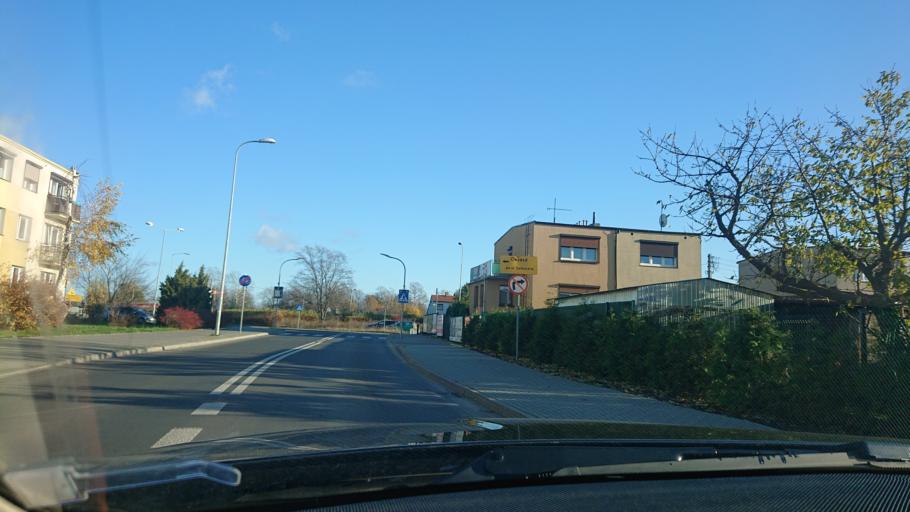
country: PL
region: Greater Poland Voivodeship
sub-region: Powiat gnieznienski
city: Gniezno
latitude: 52.5287
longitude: 17.5811
